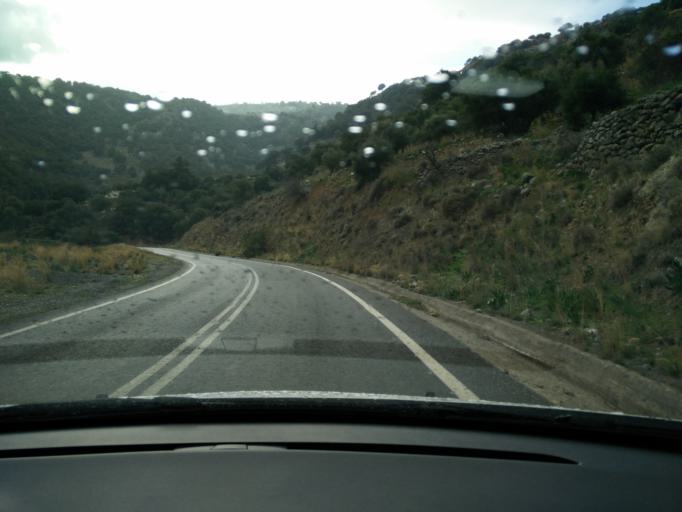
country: GR
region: Crete
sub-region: Nomos Lasithiou
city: Kritsa
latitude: 35.1495
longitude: 25.6398
